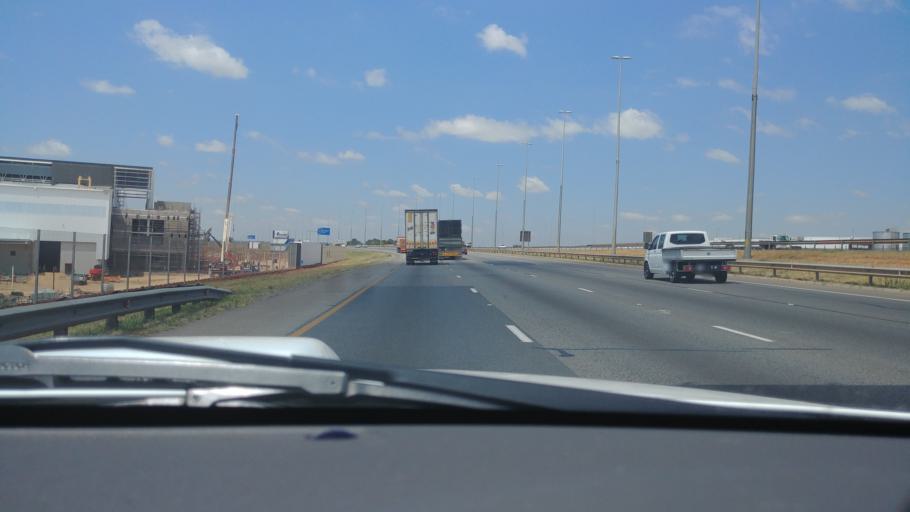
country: ZA
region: Gauteng
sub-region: Ekurhuleni Metropolitan Municipality
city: Tembisa
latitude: -26.0247
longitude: 28.2621
